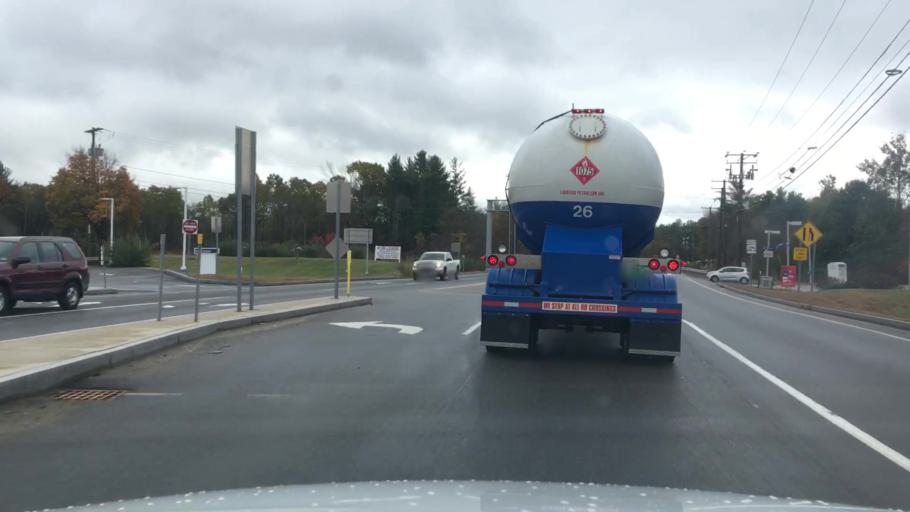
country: US
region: New Hampshire
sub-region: Strafford County
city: Lee
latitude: 43.1487
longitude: -71.0069
